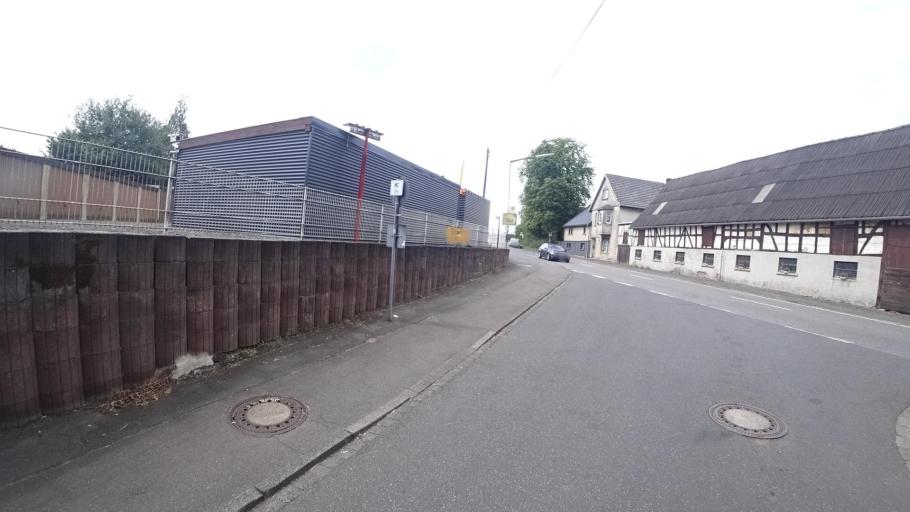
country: DE
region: Rheinland-Pfalz
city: Birnbach
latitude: 50.7081
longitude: 7.5799
